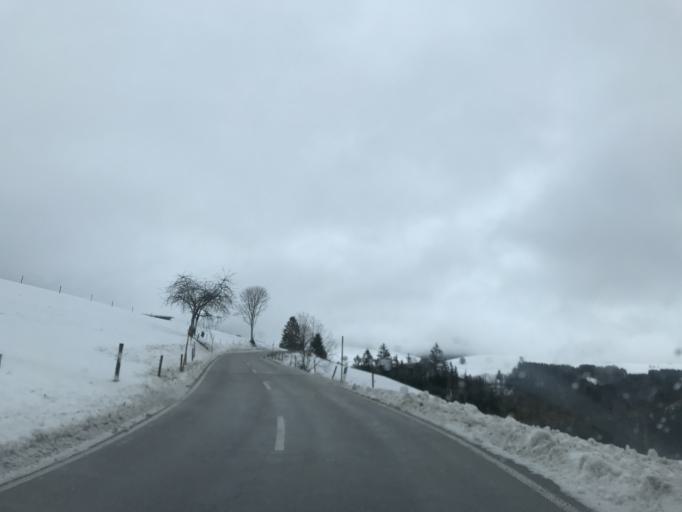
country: DE
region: Baden-Wuerttemberg
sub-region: Freiburg Region
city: Hasel
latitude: 47.6916
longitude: 7.8983
